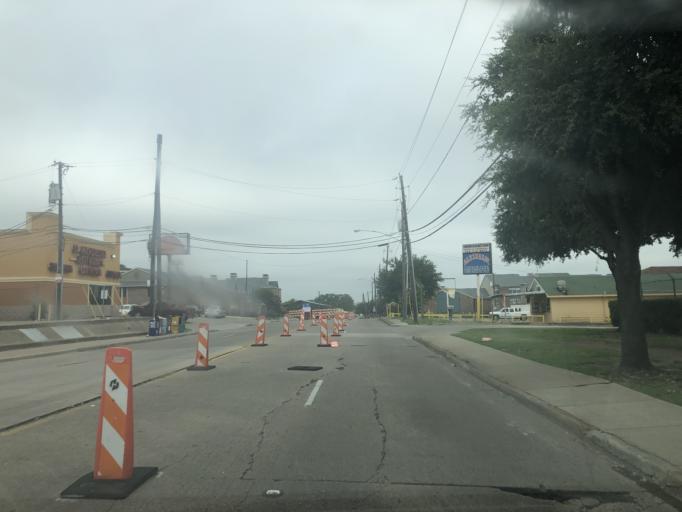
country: US
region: Texas
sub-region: Dallas County
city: Farmers Branch
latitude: 32.8665
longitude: -96.8659
